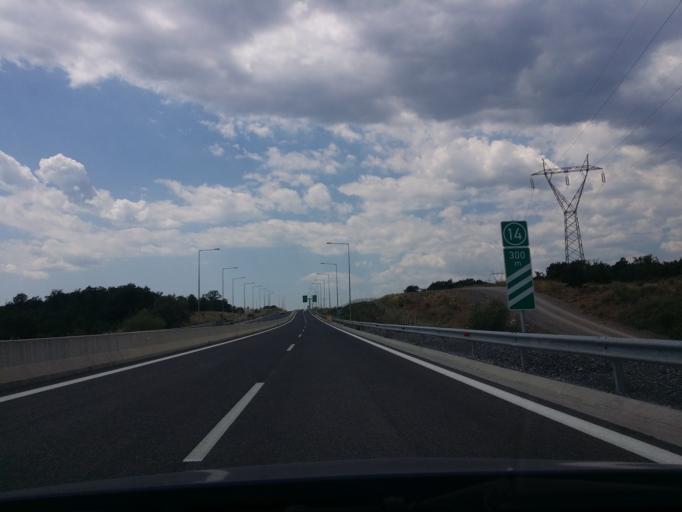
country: GR
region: Peloponnese
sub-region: Nomos Arkadias
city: Megalopoli
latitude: 37.3559
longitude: 22.1517
